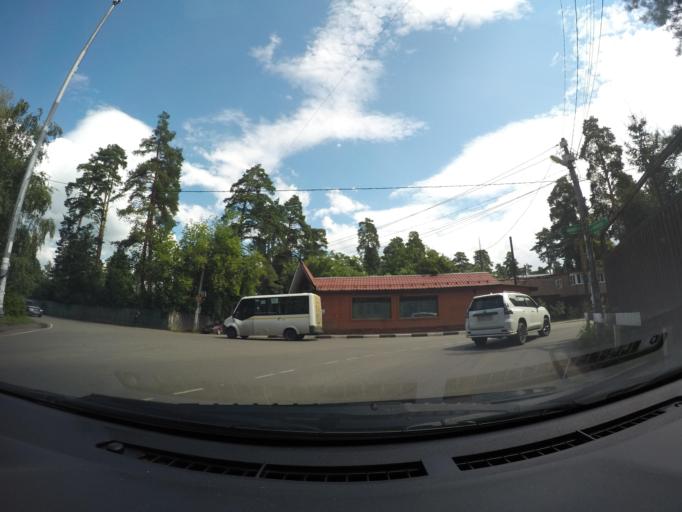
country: RU
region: Moskovskaya
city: Malakhovka
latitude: 55.6462
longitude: 38.0392
